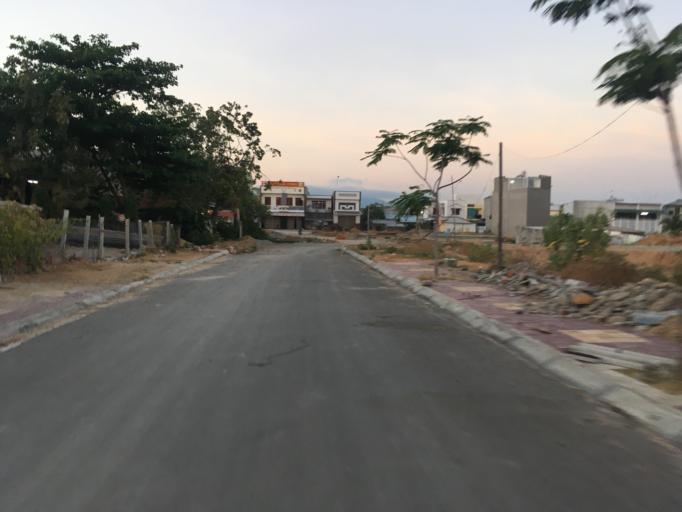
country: VN
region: Ninh Thuan
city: Phan Rang-Thap Cham
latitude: 11.5711
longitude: 108.9952
